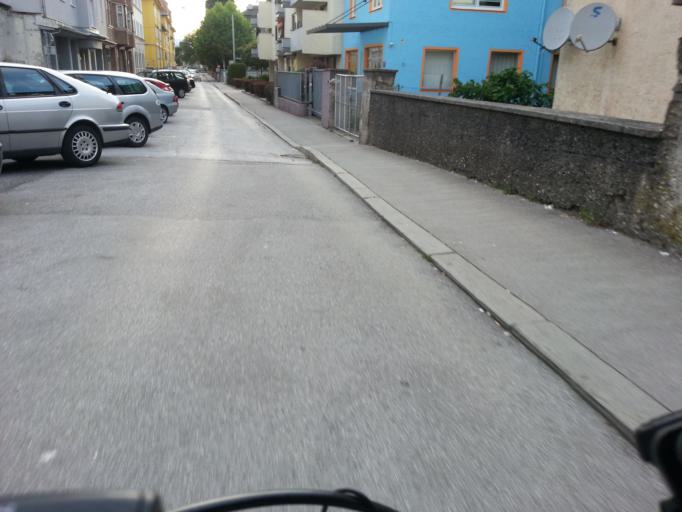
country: AT
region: Salzburg
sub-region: Salzburg Stadt
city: Salzburg
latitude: 47.8118
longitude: 13.0419
